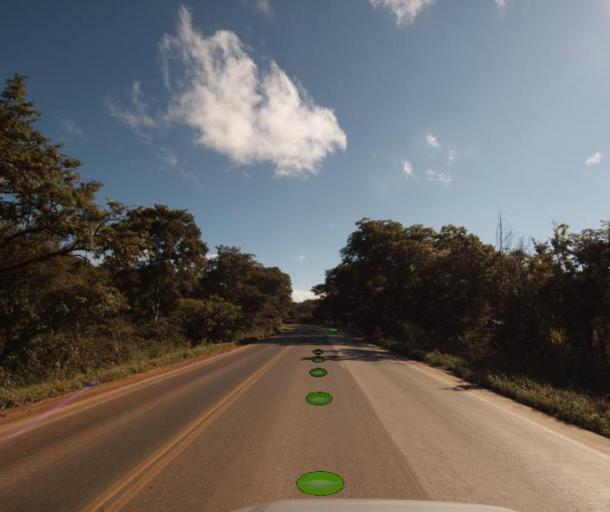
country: BR
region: Goias
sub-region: Uruacu
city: Uruacu
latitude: -14.5718
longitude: -49.1568
